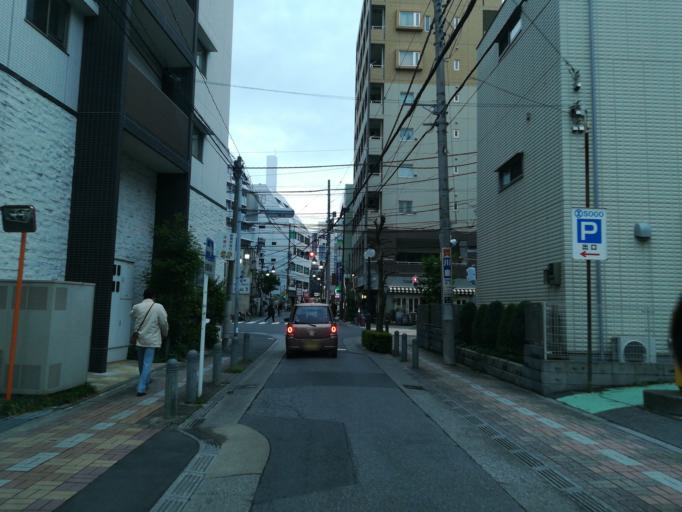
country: JP
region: Saitama
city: Kawaguchi
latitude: 35.8053
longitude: 139.7186
